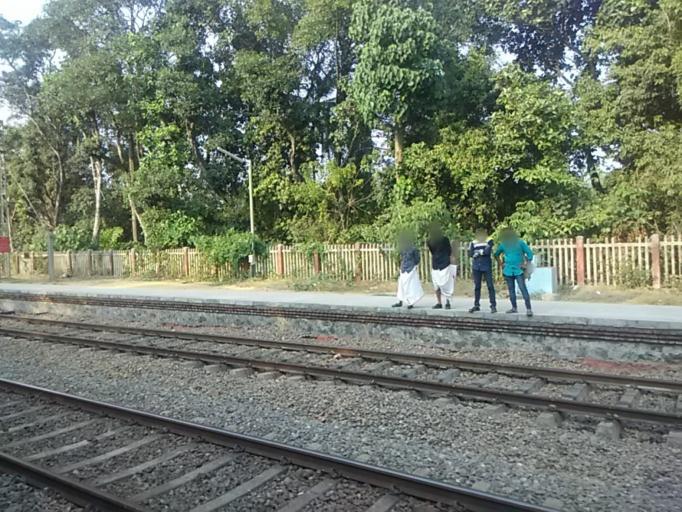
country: IN
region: Kerala
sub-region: Malappuram
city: Pariyapuram
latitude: 11.0449
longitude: 75.8614
